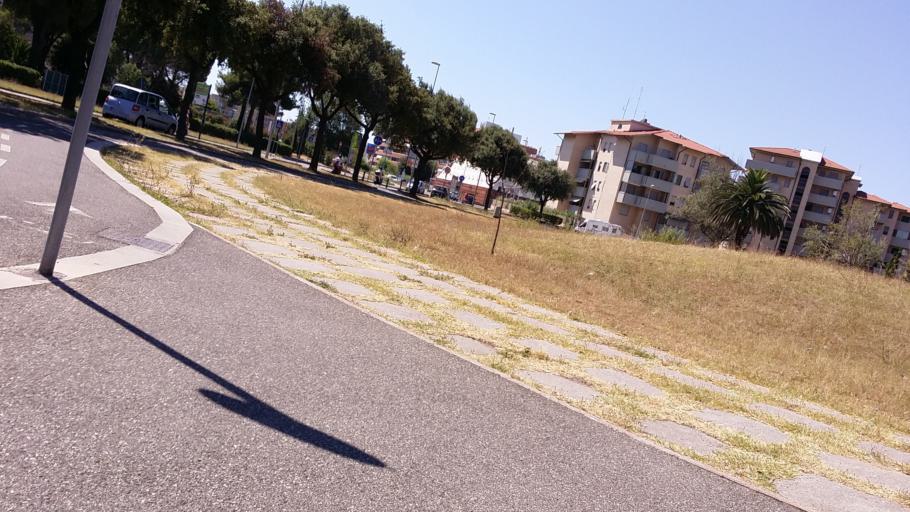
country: IT
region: Tuscany
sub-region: Provincia di Livorno
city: Livorno
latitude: 43.5432
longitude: 10.3306
